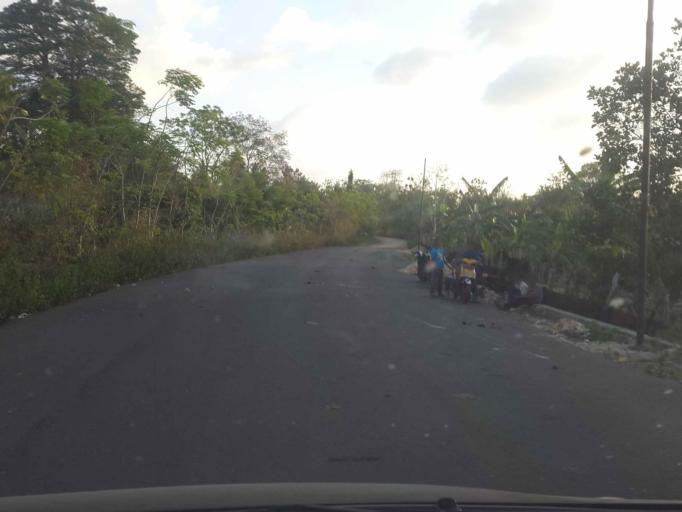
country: ID
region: South Sulawesi
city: Bantaeng
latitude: -6.1418
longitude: 120.4600
